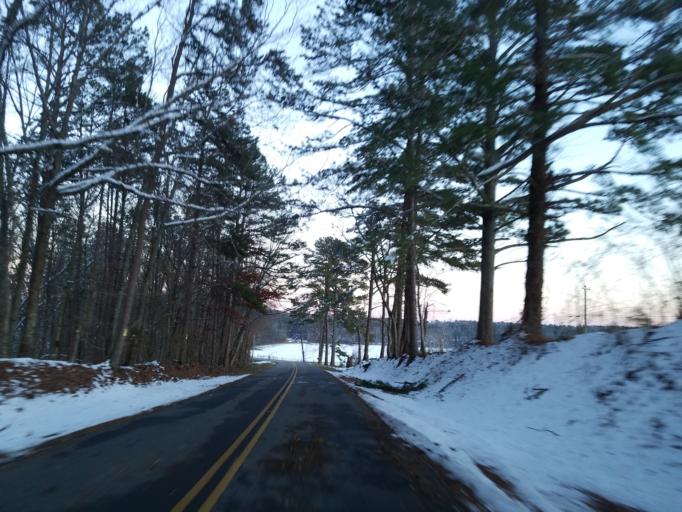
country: US
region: Georgia
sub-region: Pickens County
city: Nelson
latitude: 34.4010
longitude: -84.3807
